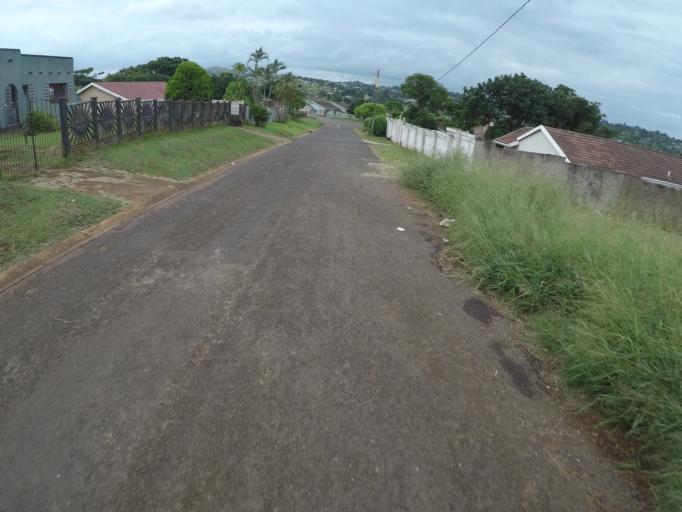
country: ZA
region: KwaZulu-Natal
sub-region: uThungulu District Municipality
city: Empangeni
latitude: -28.7693
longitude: 31.8630
